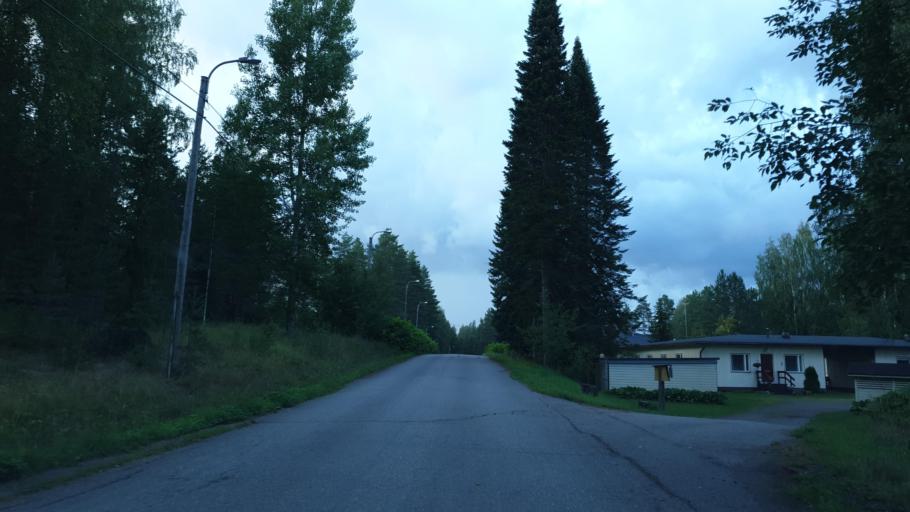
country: FI
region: Northern Savo
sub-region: Varkaus
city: Leppaevirta
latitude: 62.5846
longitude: 27.6080
